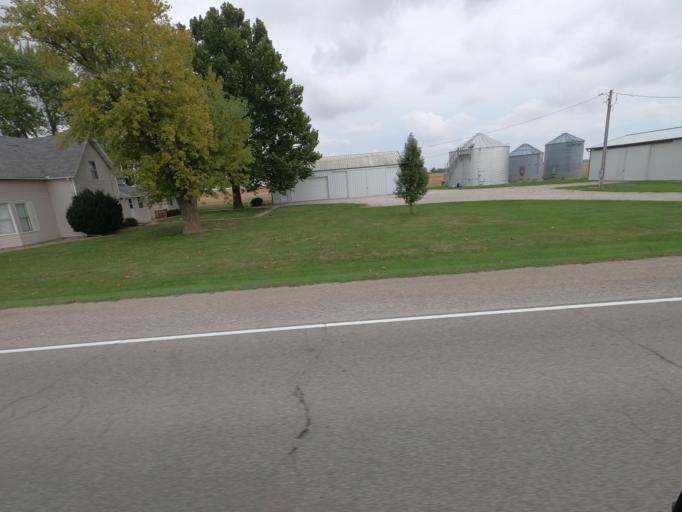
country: US
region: Iowa
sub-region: Wapello County
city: Ottumwa
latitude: 40.9815
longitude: -92.2367
